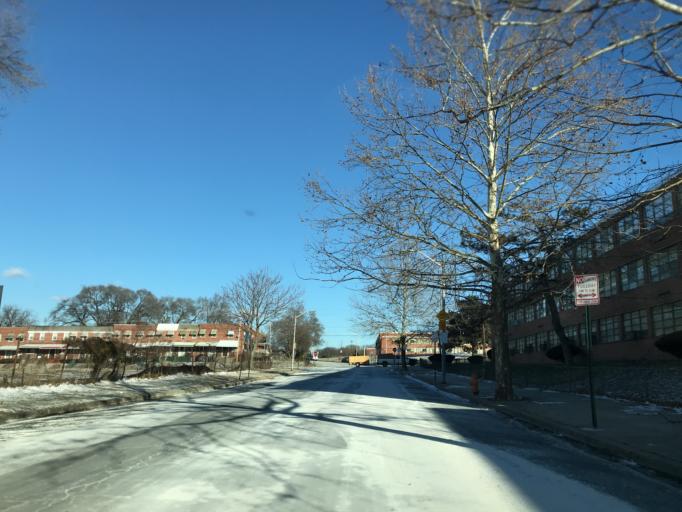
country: US
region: Maryland
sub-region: City of Baltimore
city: Baltimore
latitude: 39.2975
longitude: -76.6595
